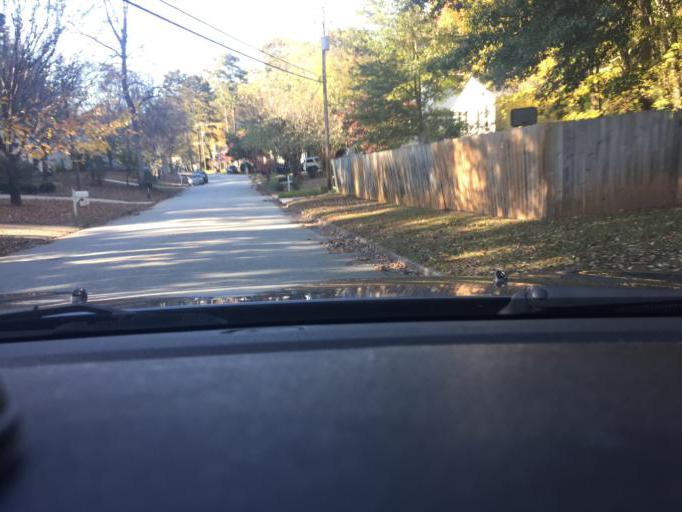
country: US
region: Georgia
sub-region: Fulton County
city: Alpharetta
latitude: 34.0305
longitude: -84.2679
